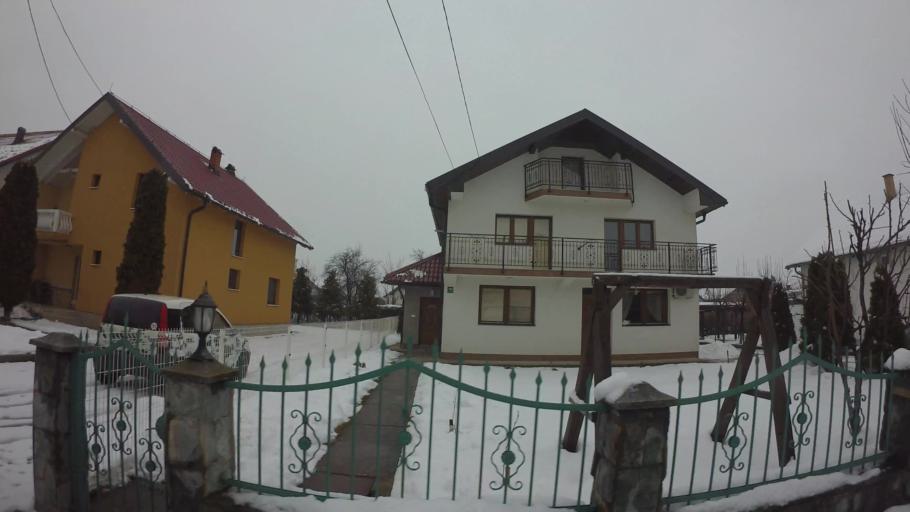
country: BA
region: Federation of Bosnia and Herzegovina
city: Hadzici
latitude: 43.8399
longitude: 18.2784
